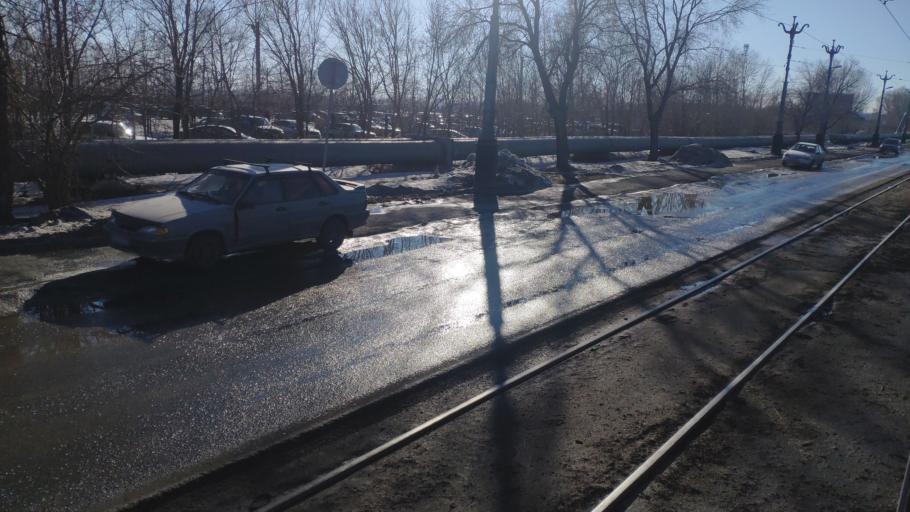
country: RU
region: Chelyabinsk
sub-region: Gorod Magnitogorsk
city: Magnitogorsk
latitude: 53.4222
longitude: 59.0289
